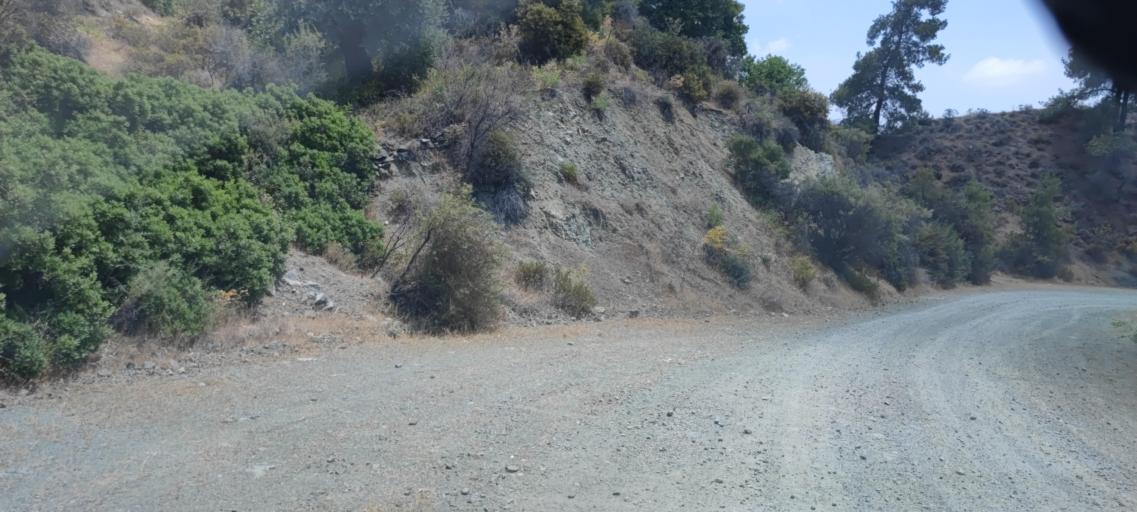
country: CY
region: Limassol
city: Pano Polemidia
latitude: 34.7991
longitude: 33.0246
